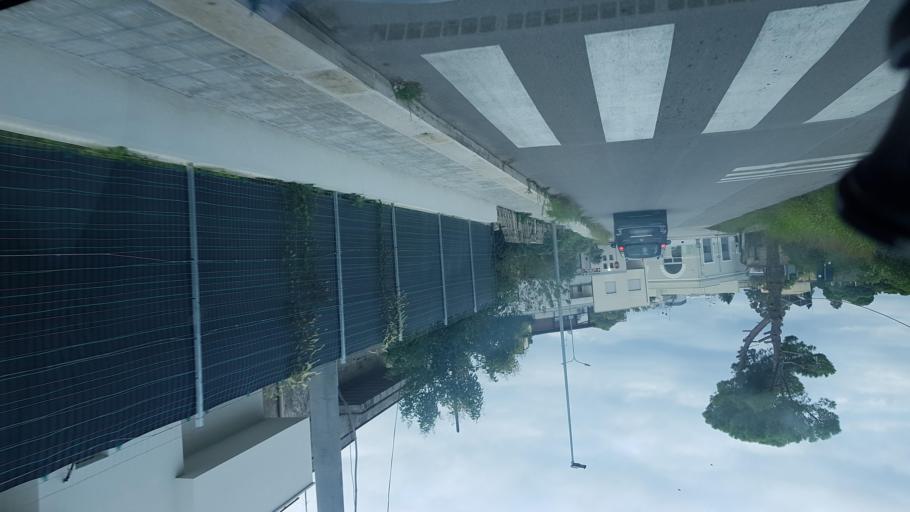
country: IT
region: Apulia
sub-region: Provincia di Brindisi
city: Oria
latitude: 40.5016
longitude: 17.6350
